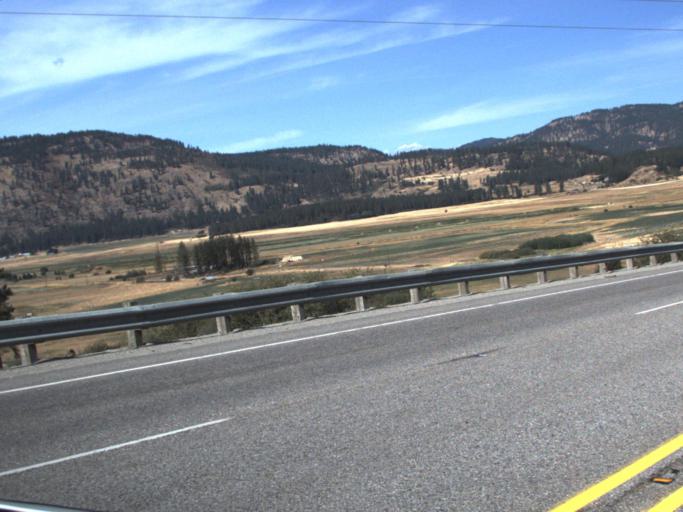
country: US
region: Washington
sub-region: Stevens County
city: Chewelah
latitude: 48.2052
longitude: -117.7147
